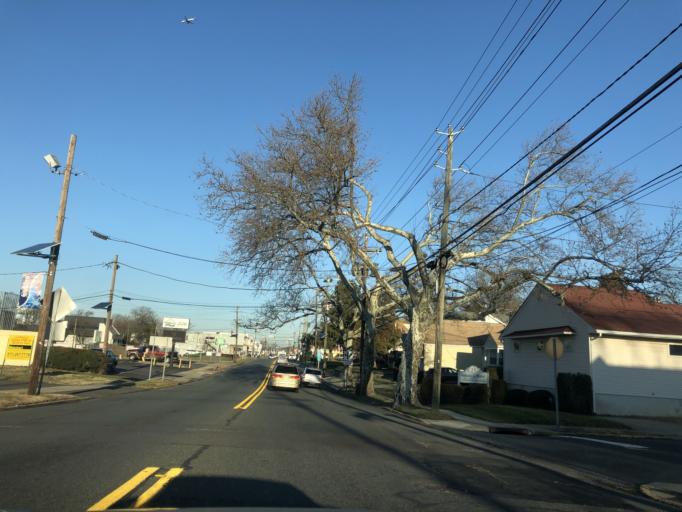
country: US
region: New Jersey
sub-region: Camden County
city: Audubon
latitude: 39.8972
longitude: -75.0720
